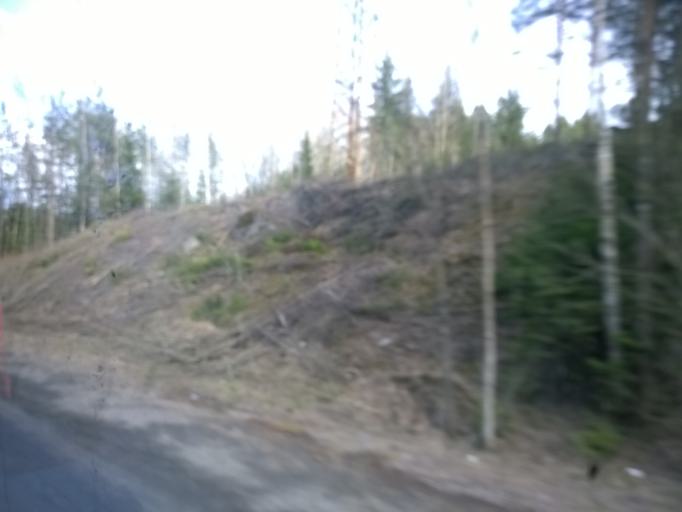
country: FI
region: Pirkanmaa
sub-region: Tampere
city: Tampere
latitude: 61.4674
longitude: 23.7746
